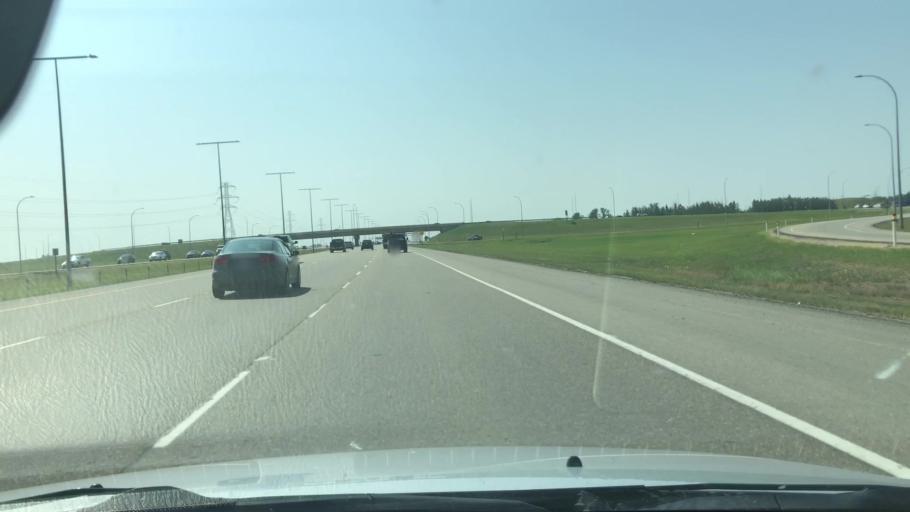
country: CA
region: Alberta
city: St. Albert
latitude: 53.5272
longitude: -113.6599
